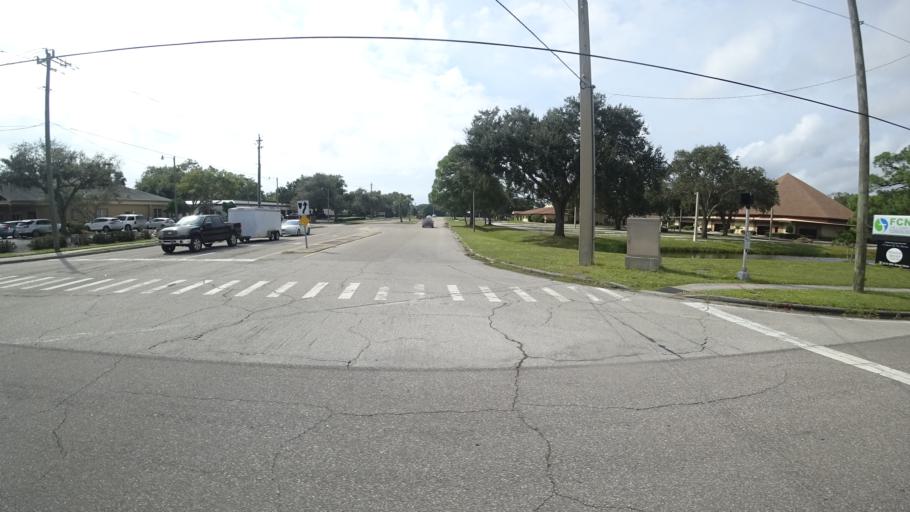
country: US
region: Florida
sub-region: Manatee County
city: West Bradenton
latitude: 27.4851
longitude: -82.6205
